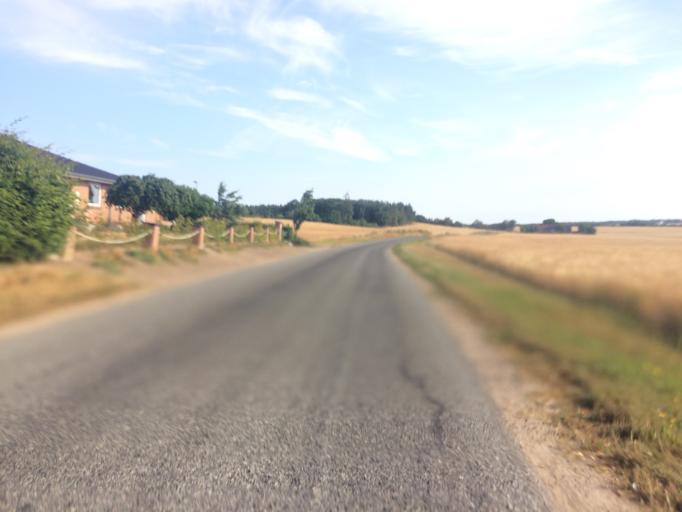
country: DK
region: Central Jutland
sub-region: Holstebro Kommune
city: Vinderup
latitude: 56.6030
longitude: 8.7607
